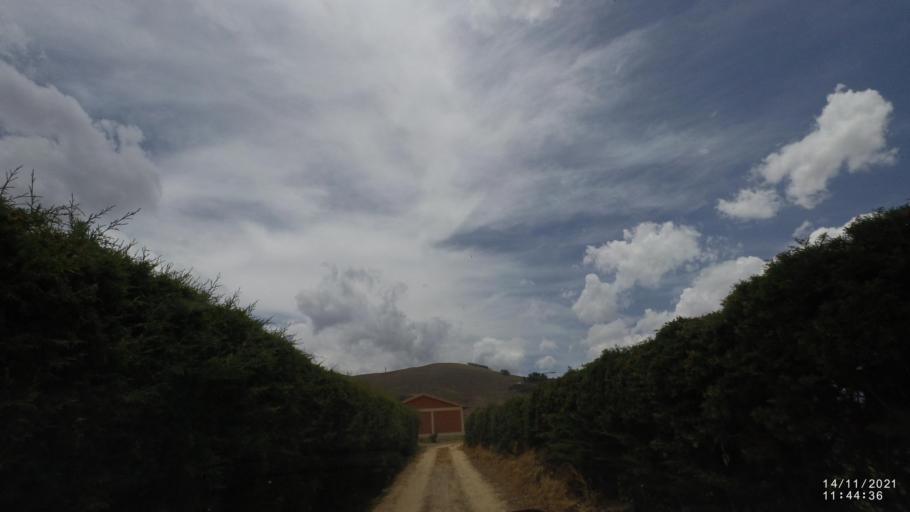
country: BO
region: Cochabamba
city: Colomi
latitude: -17.3528
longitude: -65.9906
